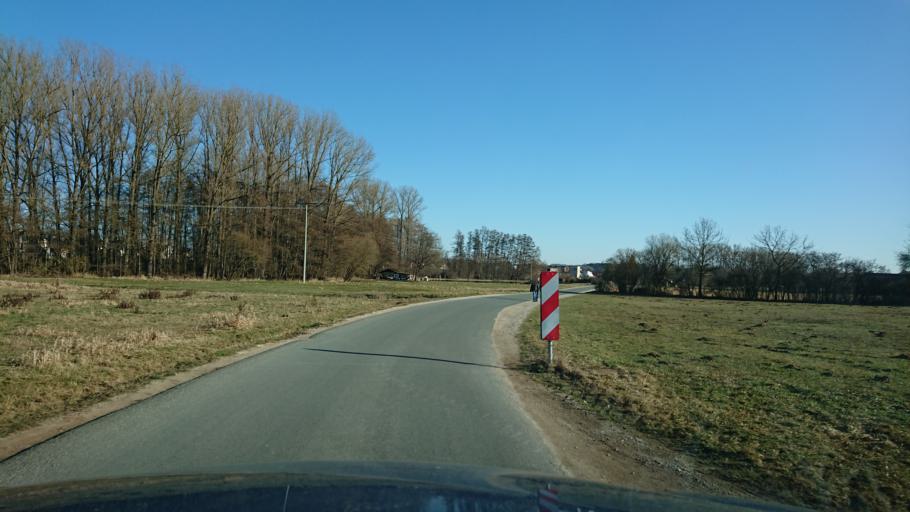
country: DE
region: Bavaria
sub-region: Upper Franconia
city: Neunkirchen am Brand
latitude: 49.6137
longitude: 11.1157
